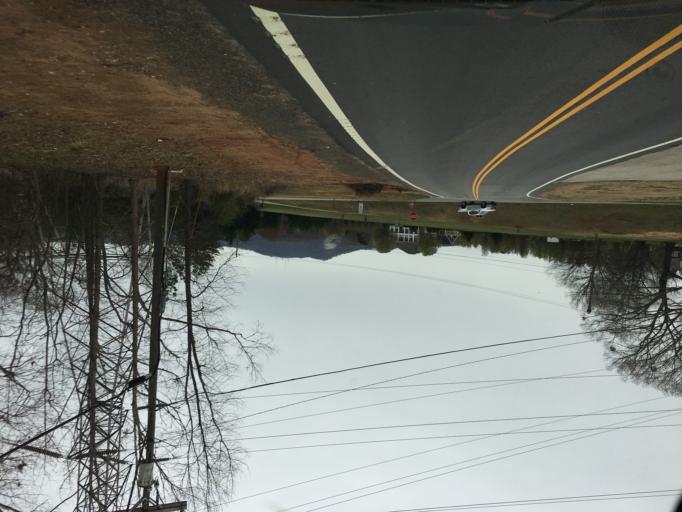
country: US
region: South Carolina
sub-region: Greenville County
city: Berea
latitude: 34.9180
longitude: -82.4691
